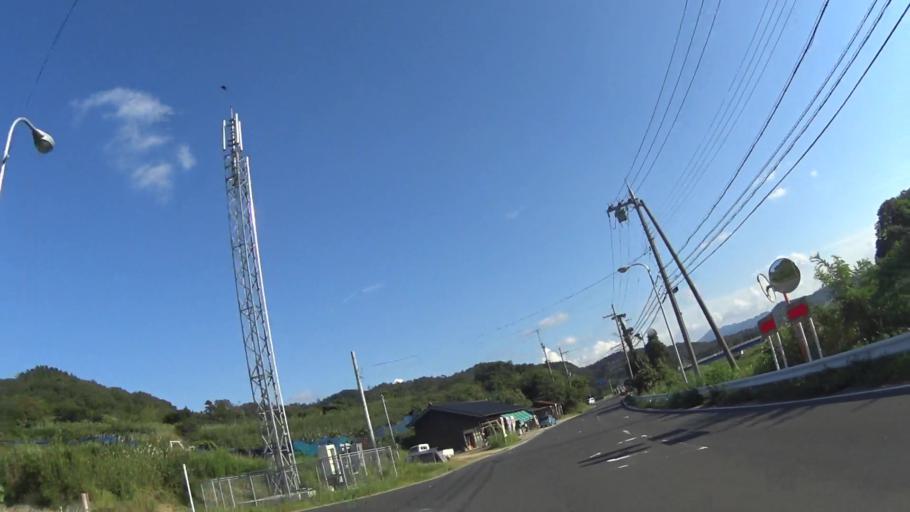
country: JP
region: Hyogo
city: Toyooka
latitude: 35.6426
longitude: 134.9449
